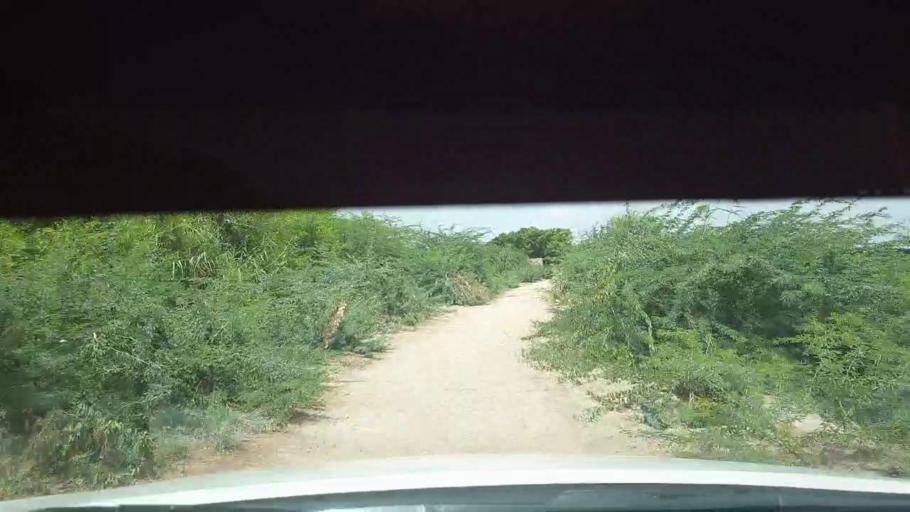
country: PK
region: Sindh
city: Kadhan
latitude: 24.5470
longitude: 68.9670
